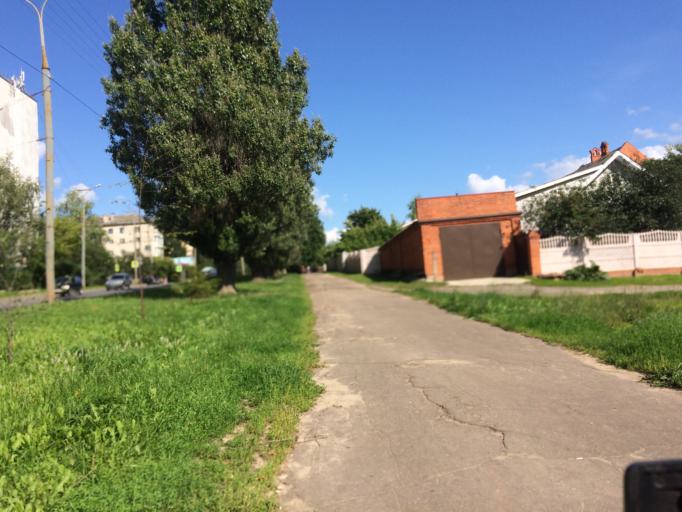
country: RU
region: Mariy-El
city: Yoshkar-Ola
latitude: 56.6217
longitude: 47.9435
